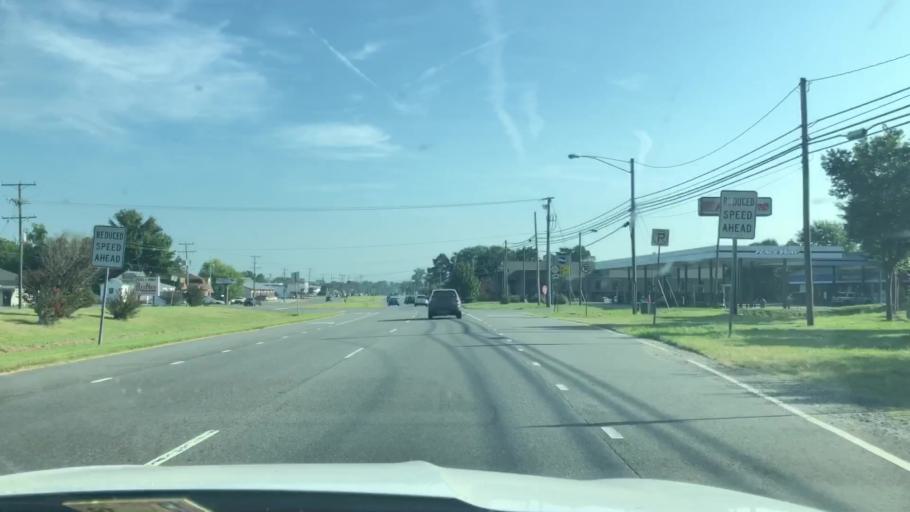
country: US
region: Virginia
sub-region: Essex County
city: Tappahannock
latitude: 37.9100
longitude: -76.8620
